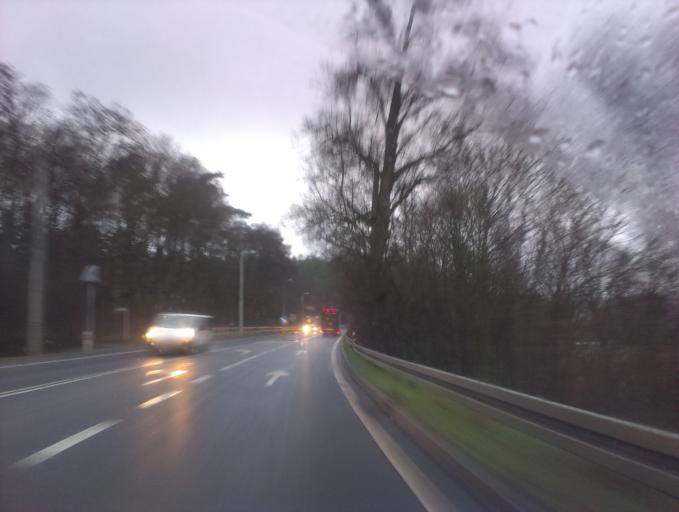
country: PL
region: Greater Poland Voivodeship
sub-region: Powiat chodzieski
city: Chodziez
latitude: 52.9778
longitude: 16.9266
